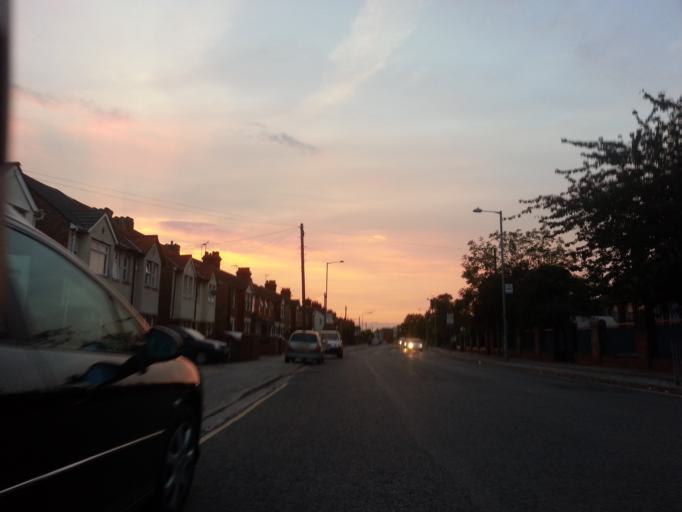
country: GB
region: England
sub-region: Suffolk
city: Ipswich
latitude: 52.0415
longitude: 1.1842
